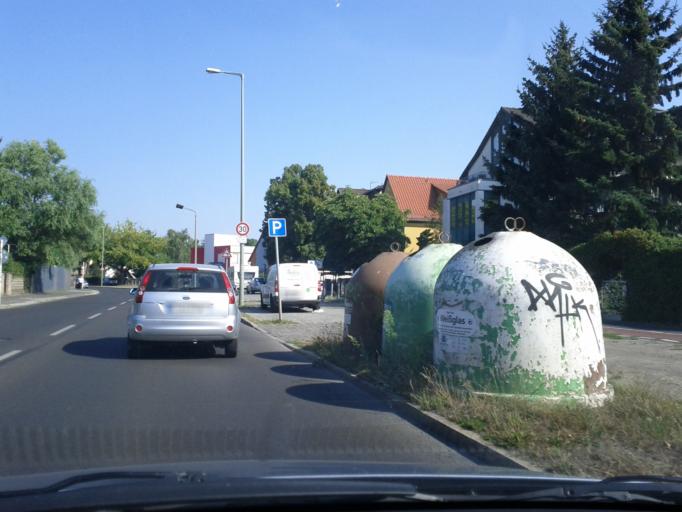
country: DE
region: Berlin
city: Kopenick Bezirk
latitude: 52.4690
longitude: 13.5737
